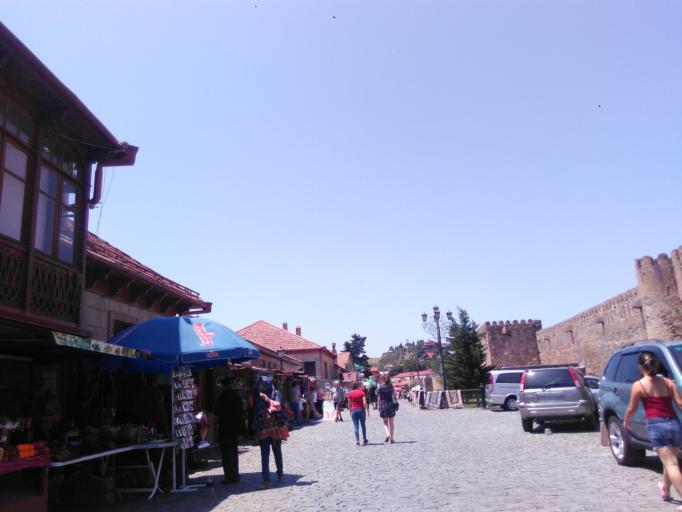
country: GE
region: Mtskheta-Mtianeti
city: Mtskheta
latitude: 41.8418
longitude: 44.7216
